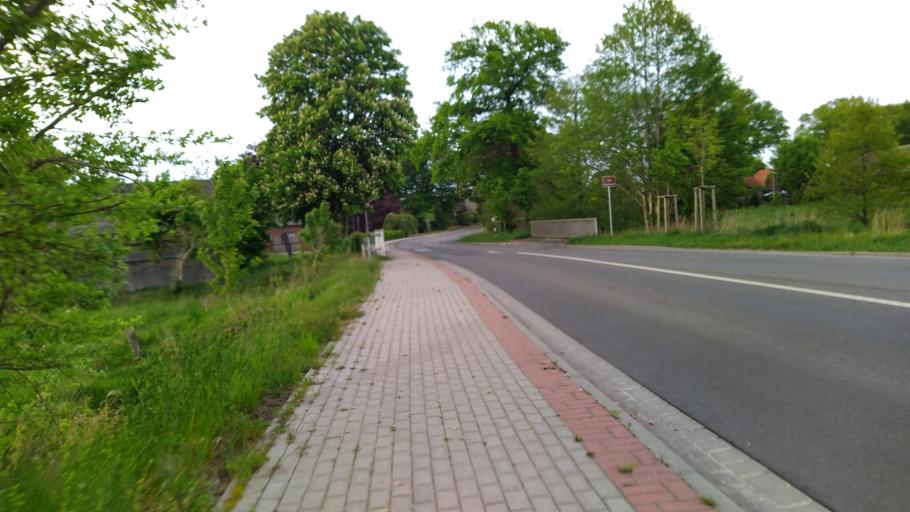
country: DE
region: Lower Saxony
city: Ahlerstedt
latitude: 53.4021
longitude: 9.4057
